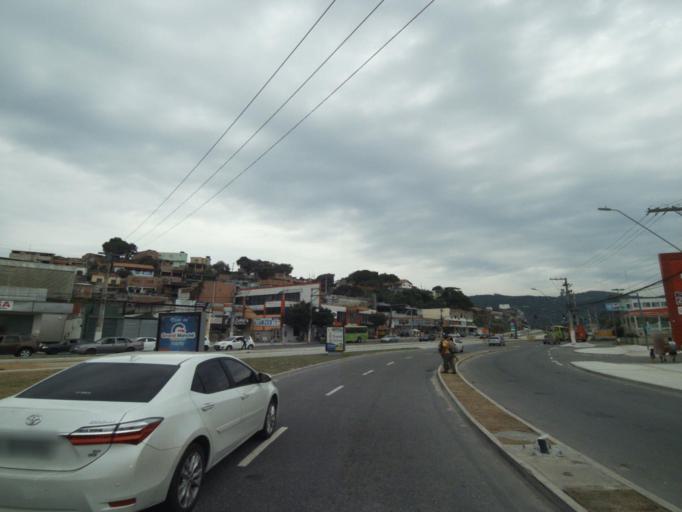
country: BR
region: Rio de Janeiro
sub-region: Niteroi
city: Niteroi
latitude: -22.9415
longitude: -43.0572
